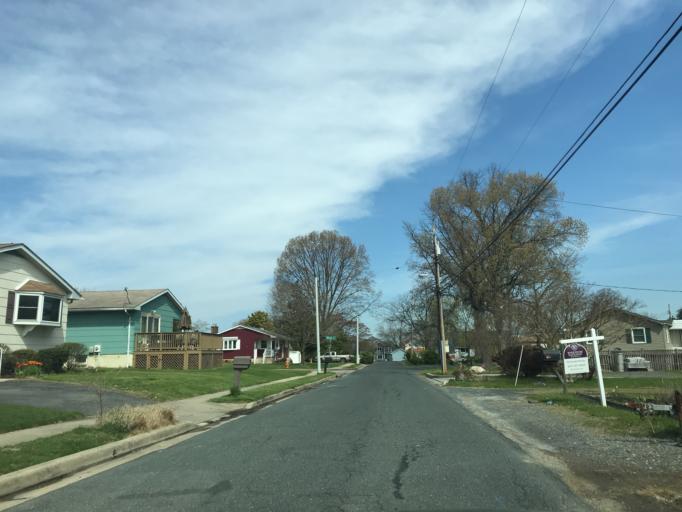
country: US
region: Maryland
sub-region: Baltimore County
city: Middle River
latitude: 39.3103
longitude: -76.4257
